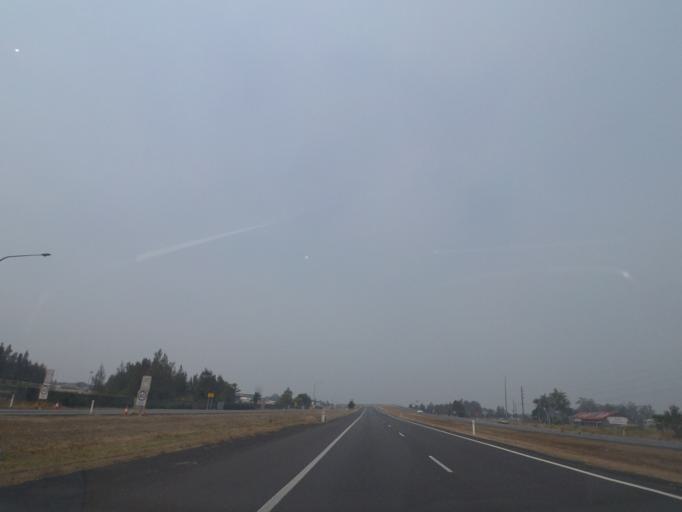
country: AU
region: New South Wales
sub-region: Ballina
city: Ballina
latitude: -28.8628
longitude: 153.5146
